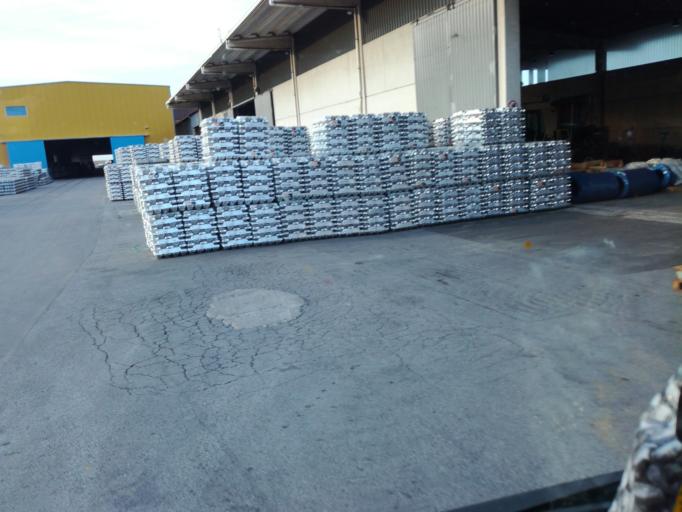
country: IT
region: Liguria
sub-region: Provincia di Genova
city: San Teodoro
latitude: 44.4062
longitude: 8.8936
